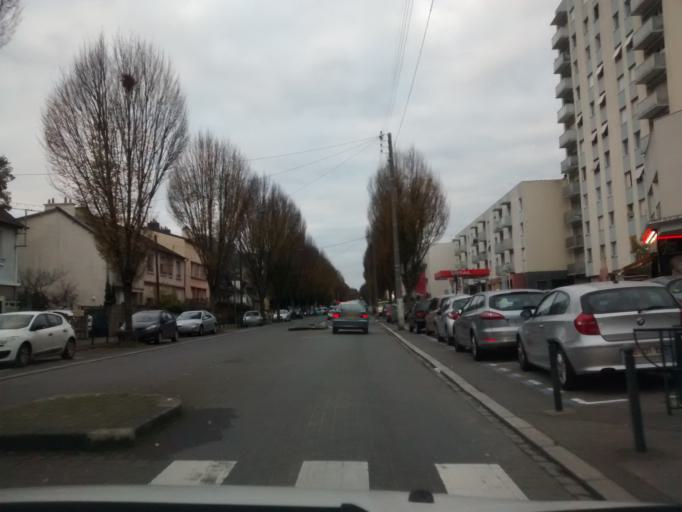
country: FR
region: Brittany
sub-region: Departement d'Ille-et-Vilaine
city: Rennes
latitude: 48.0992
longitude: -1.6530
